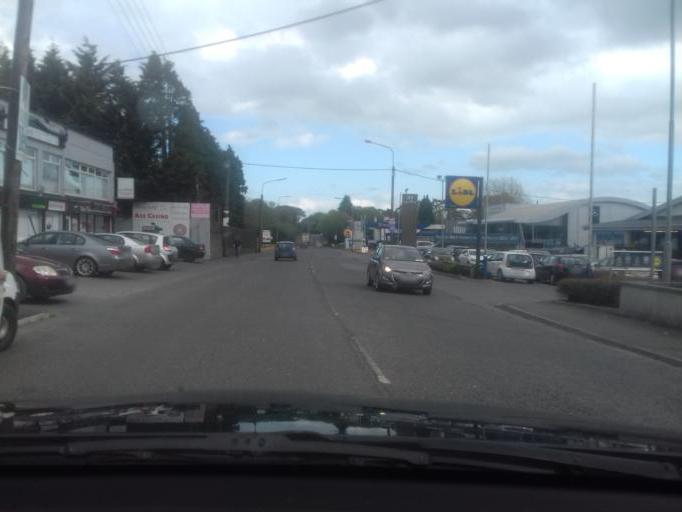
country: IE
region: Leinster
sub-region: Kildare
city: Kildare
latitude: 53.1554
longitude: -6.9055
